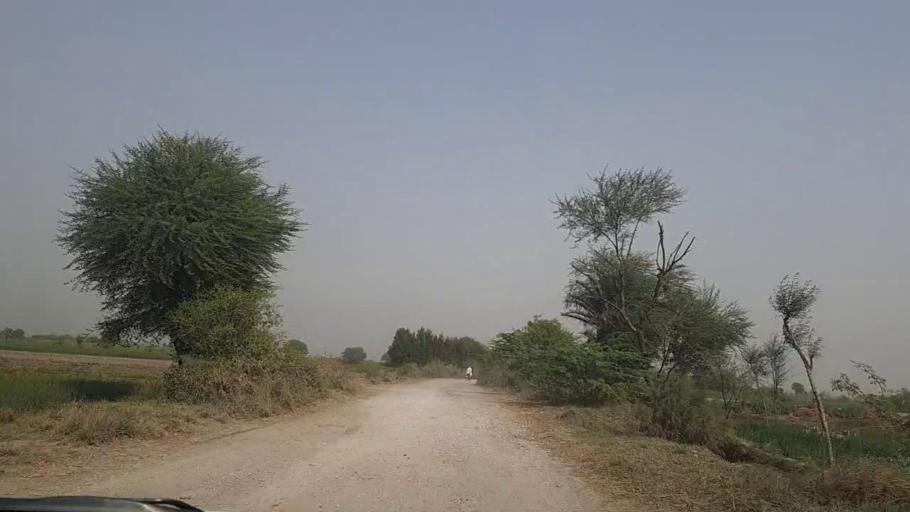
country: PK
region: Sindh
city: Pithoro
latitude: 25.4769
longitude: 69.2238
